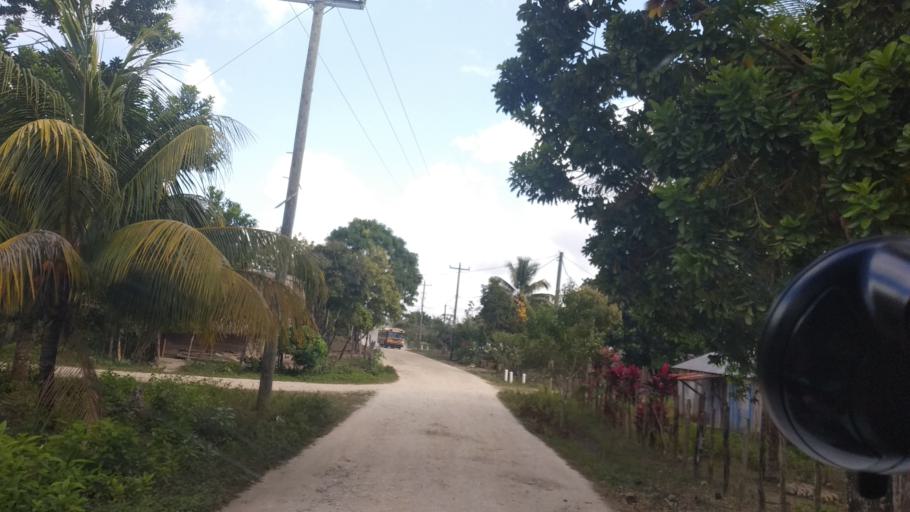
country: BZ
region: Stann Creek
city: Placencia
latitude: 16.4709
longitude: -88.6244
